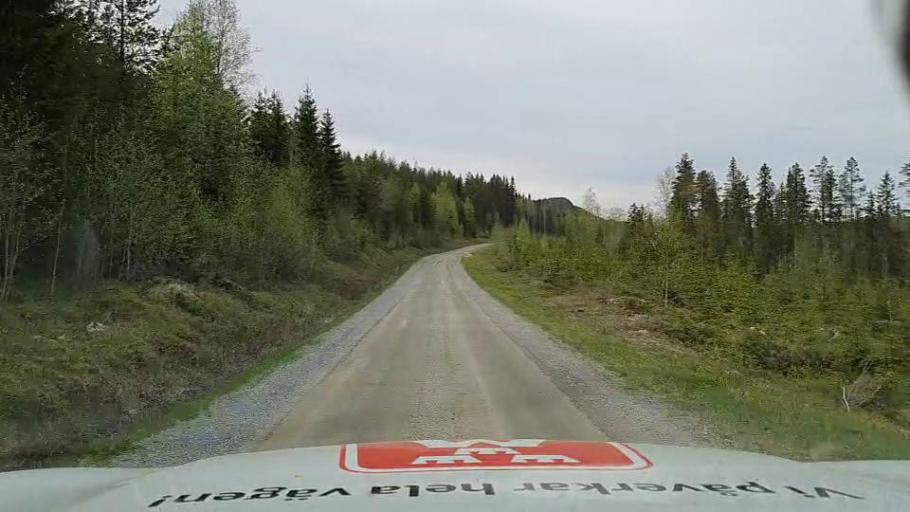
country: SE
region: Jaemtland
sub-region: Bergs Kommun
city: Hoverberg
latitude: 62.5447
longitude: 14.8997
